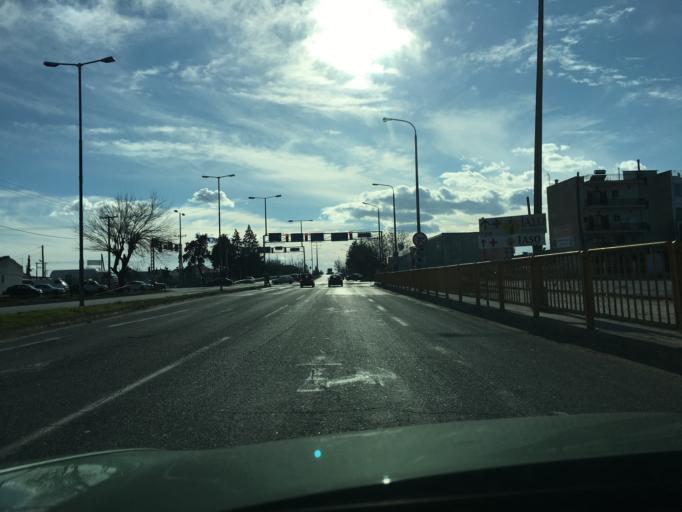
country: GR
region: Thessaly
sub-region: Nomos Larisis
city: Larisa
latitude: 39.6344
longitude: 22.4353
